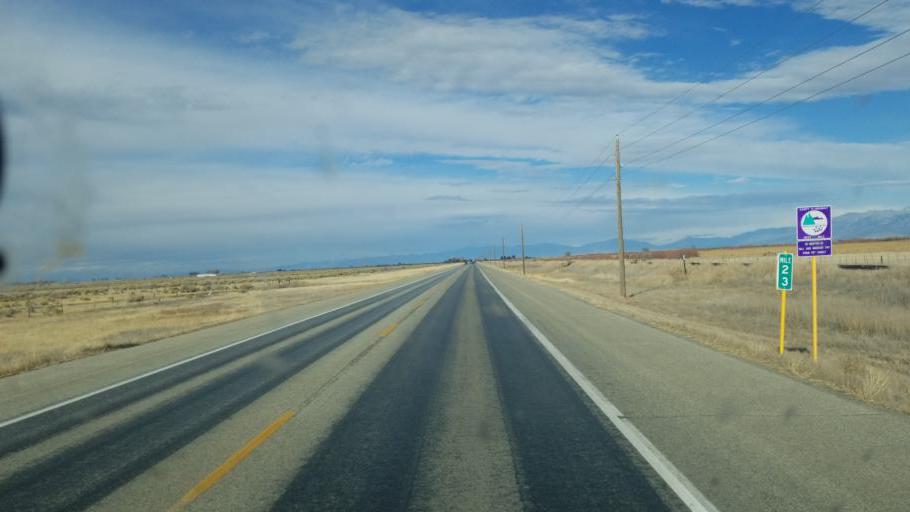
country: US
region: Colorado
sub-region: Alamosa County
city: Alamosa
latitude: 37.3195
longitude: -105.9490
